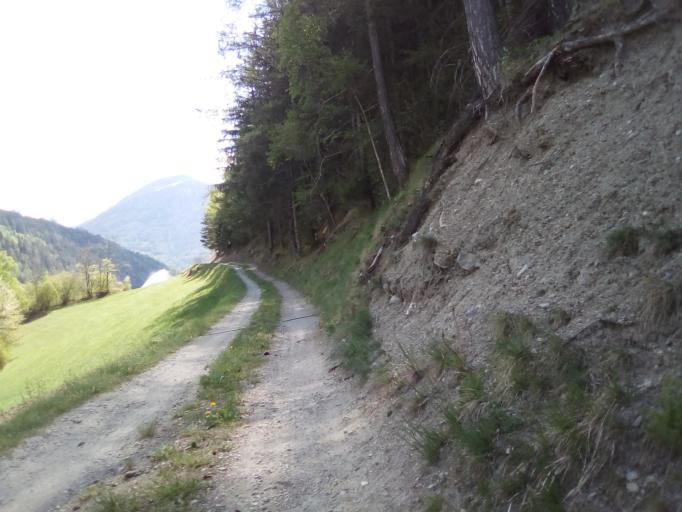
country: CH
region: Valais
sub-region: Entremont District
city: Orsieres
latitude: 46.0535
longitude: 7.1474
